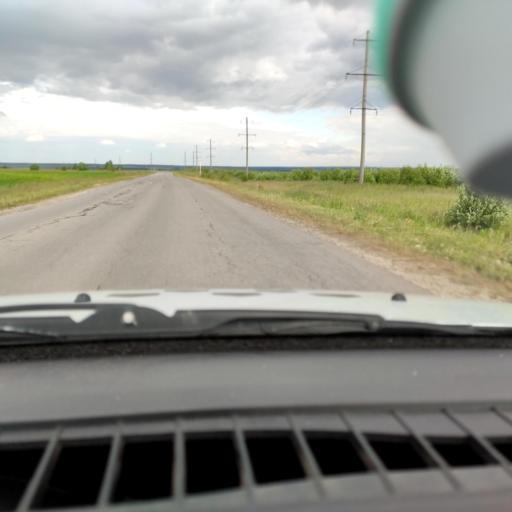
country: RU
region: Perm
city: Orda
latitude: 57.1895
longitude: 56.8697
